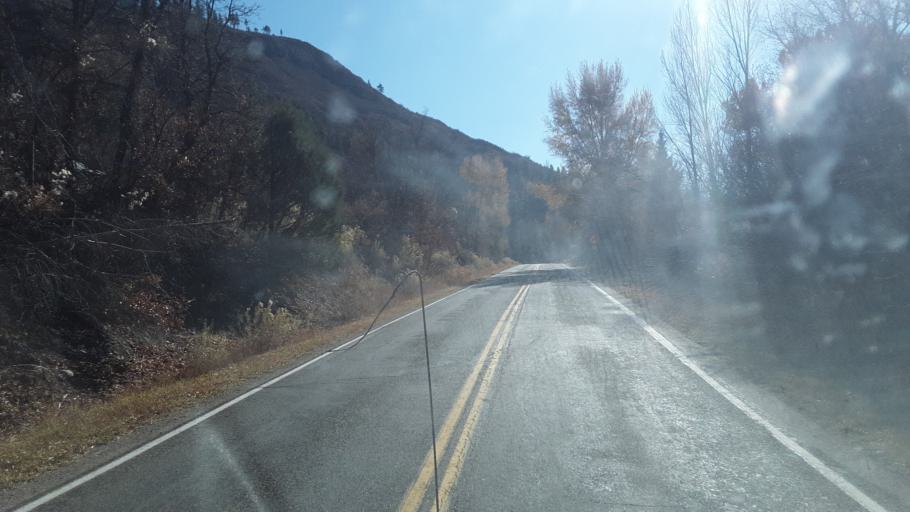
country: US
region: Colorado
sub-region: La Plata County
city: Durango
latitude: 37.4213
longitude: -107.7998
